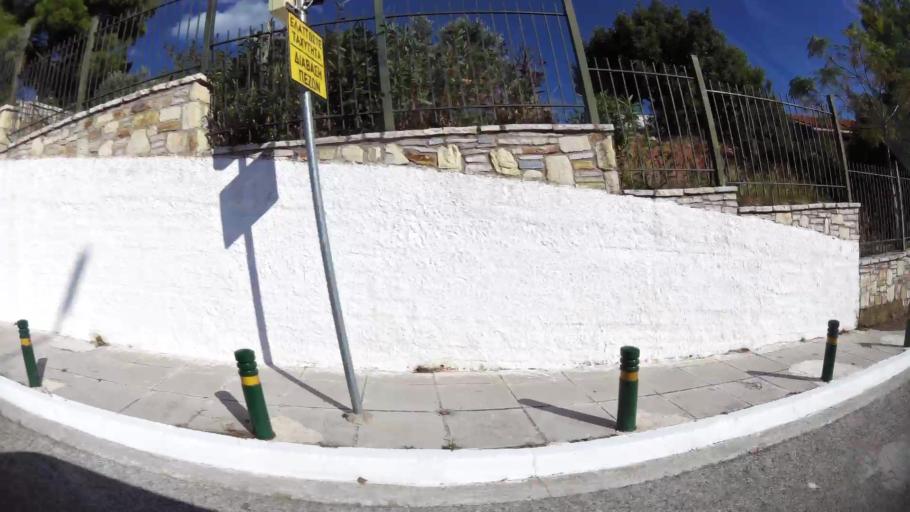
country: GR
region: Attica
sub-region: Nomarchia Anatolikis Attikis
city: Anthousa
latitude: 38.0258
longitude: 23.8733
